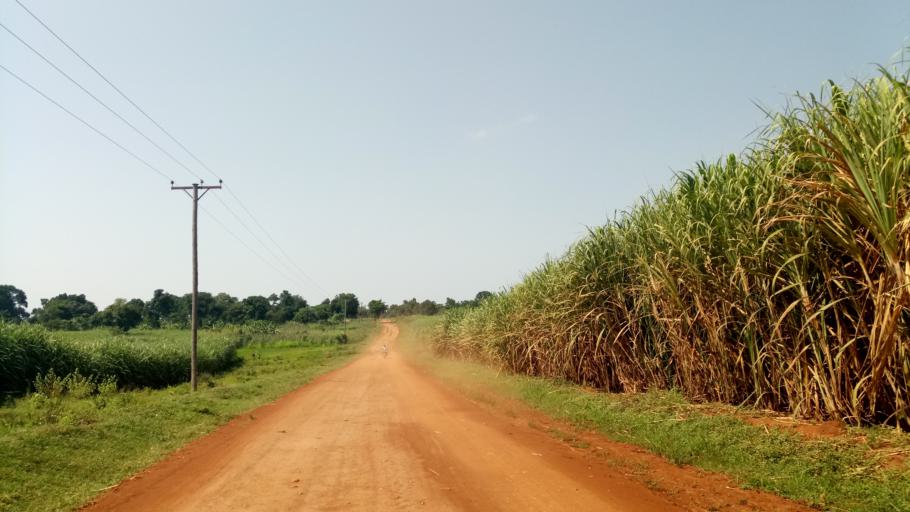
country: UG
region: Eastern Region
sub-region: Kaliro District
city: Kaliro
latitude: 0.9741
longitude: 33.4611
